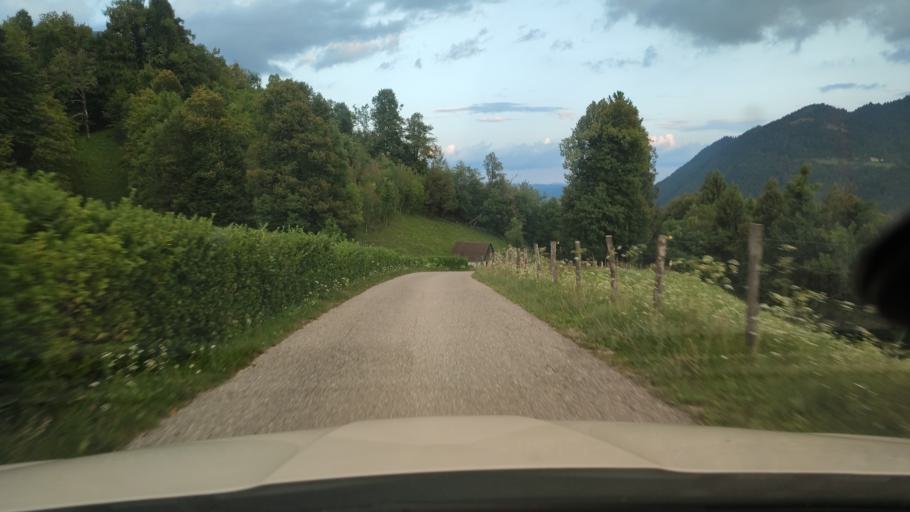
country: IT
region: Friuli Venezia Giulia
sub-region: Provincia di Udine
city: Cras
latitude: 46.2199
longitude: 13.6412
